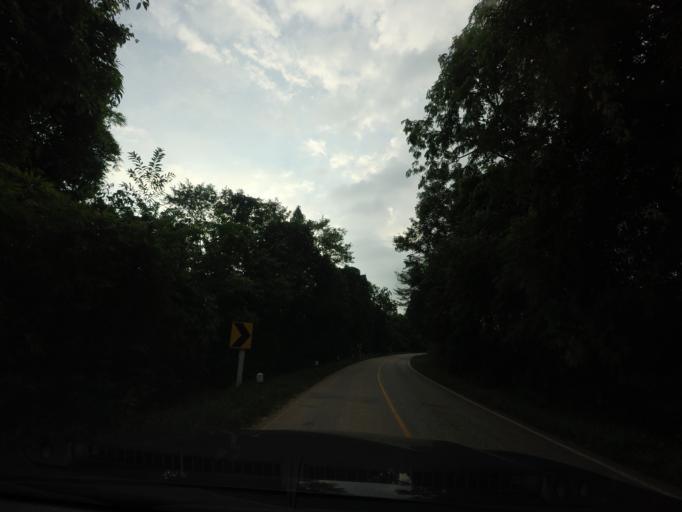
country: TH
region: Loei
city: Dan Sai
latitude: 17.3301
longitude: 101.1068
